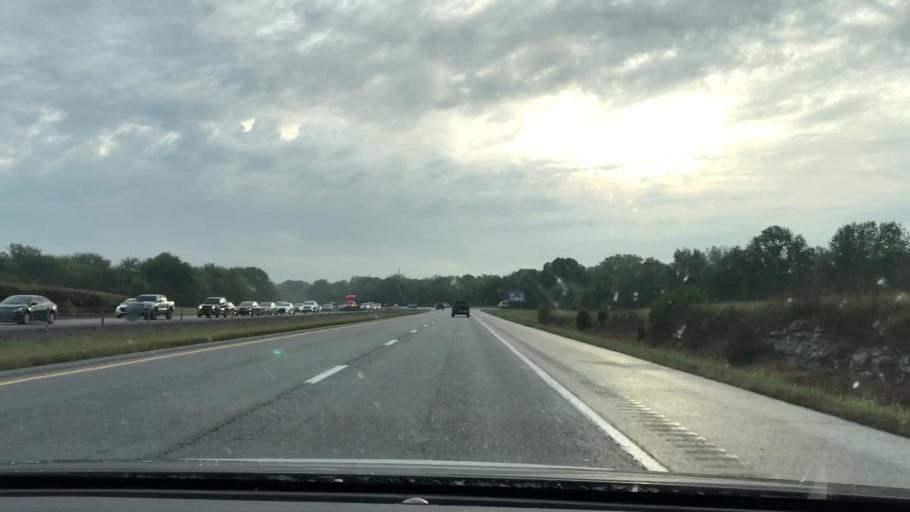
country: US
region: Tennessee
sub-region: Sumner County
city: Hendersonville
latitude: 36.3302
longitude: -86.6170
